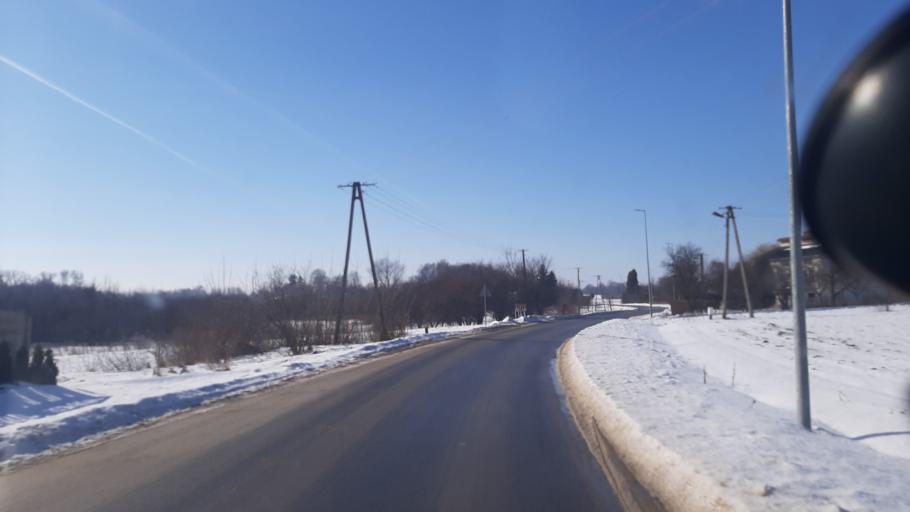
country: PL
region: Lublin Voivodeship
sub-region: Powiat lubelski
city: Garbow
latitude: 51.2939
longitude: 22.3009
